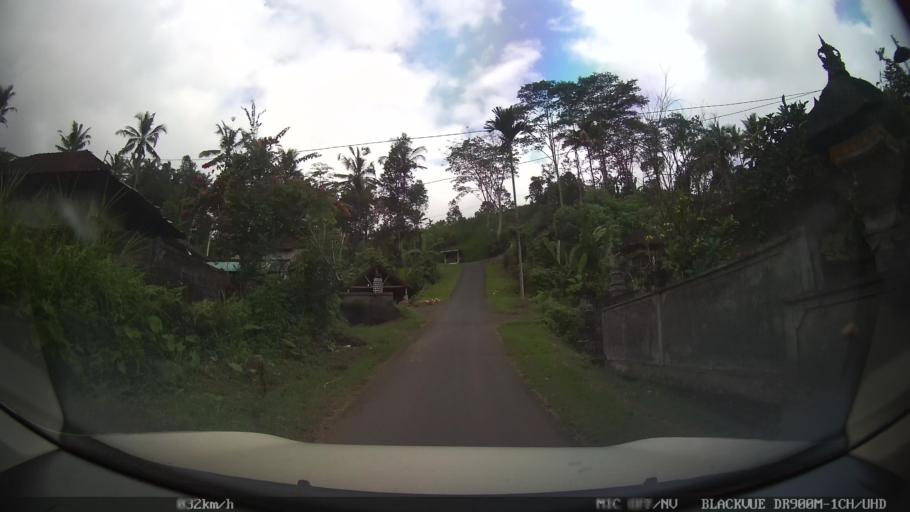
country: ID
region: Bali
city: Banjar Wangsian
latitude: -8.4594
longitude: 115.4150
